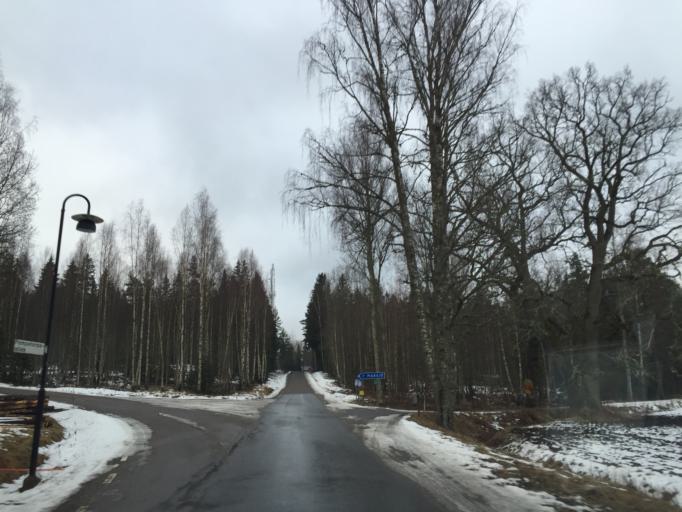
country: SE
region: Soedermanland
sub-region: Vingakers Kommun
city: Vingaker
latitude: 59.0201
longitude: 15.6771
